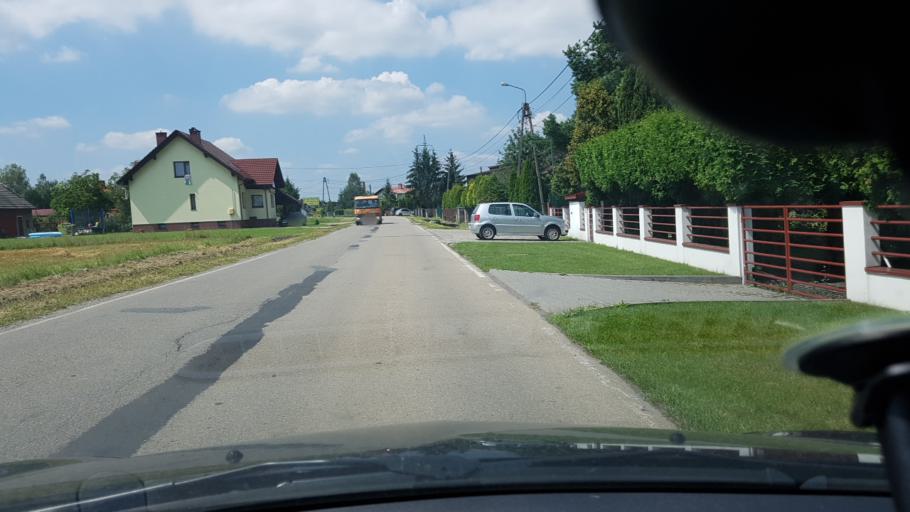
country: PL
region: Lesser Poland Voivodeship
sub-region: Powiat oswiecimski
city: Babice
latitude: 50.0555
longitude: 19.1952
